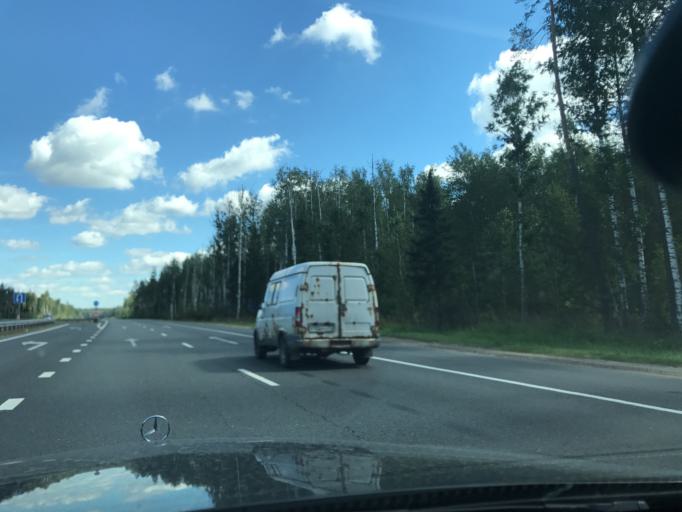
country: RU
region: Vladimir
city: Sudogda
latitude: 56.1374
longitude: 40.8923
